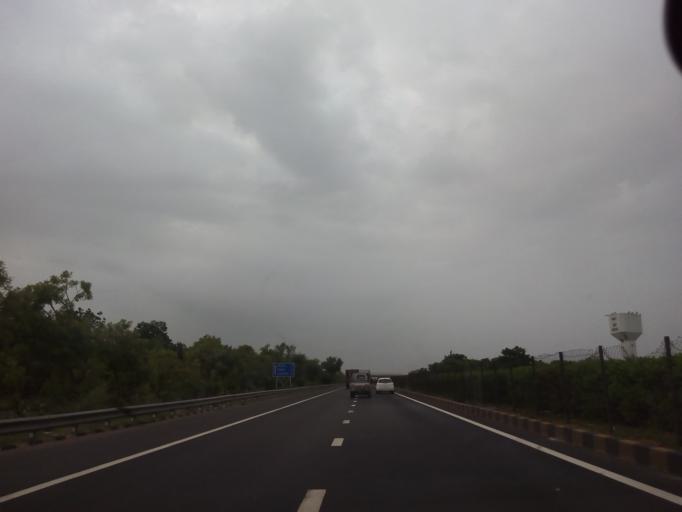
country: IN
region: Gujarat
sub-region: Kheda
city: Mahemdavad
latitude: 22.8630
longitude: 72.8068
